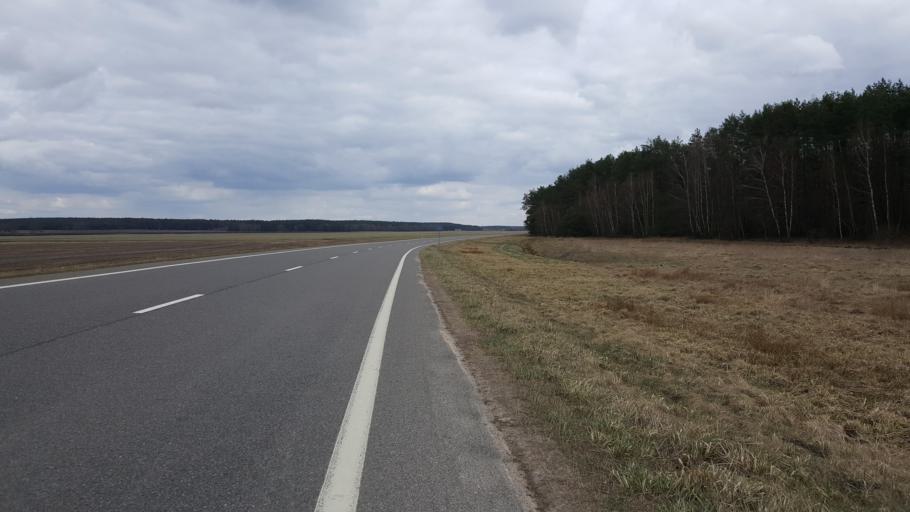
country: BY
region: Brest
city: Kamyanyuki
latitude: 52.5077
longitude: 23.7470
